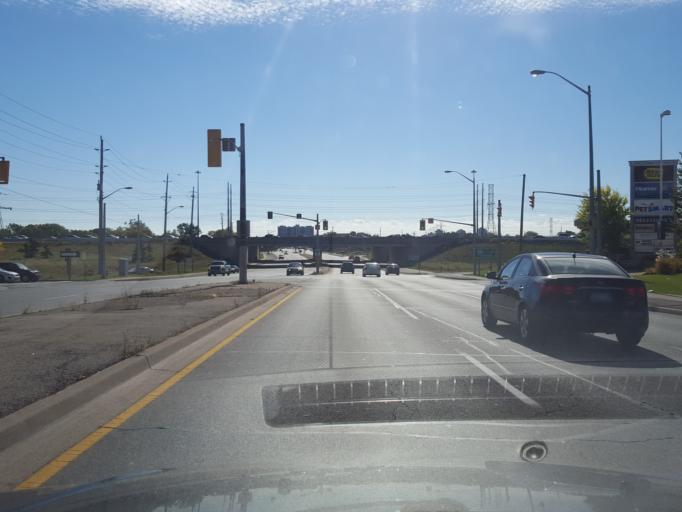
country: CA
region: Ontario
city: Burlington
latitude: 43.3430
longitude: -79.8241
